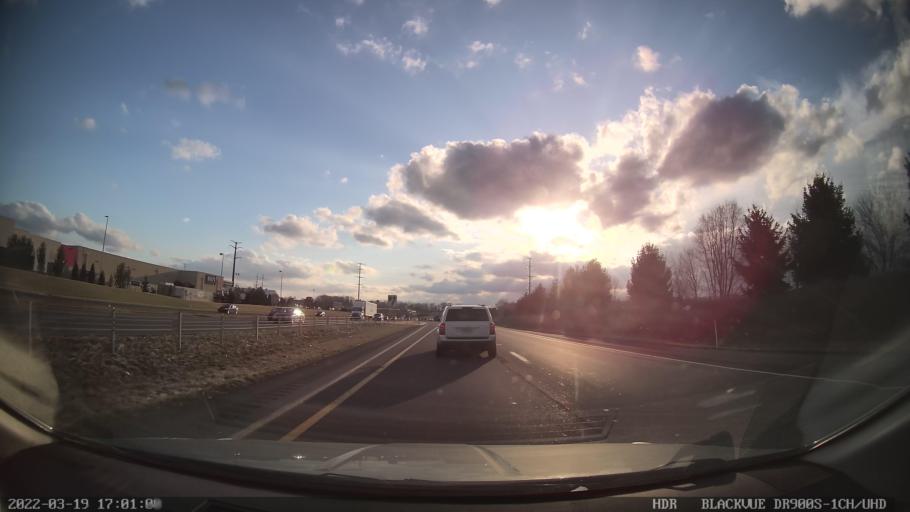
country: US
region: Pennsylvania
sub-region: Lehigh County
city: Wescosville
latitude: 40.5676
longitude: -75.5616
